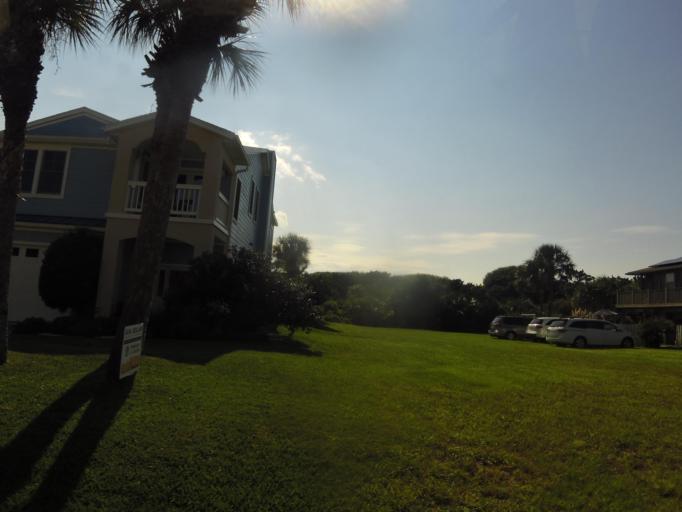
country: US
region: Florida
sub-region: Nassau County
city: Fernandina Beach
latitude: 30.6873
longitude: -81.4303
